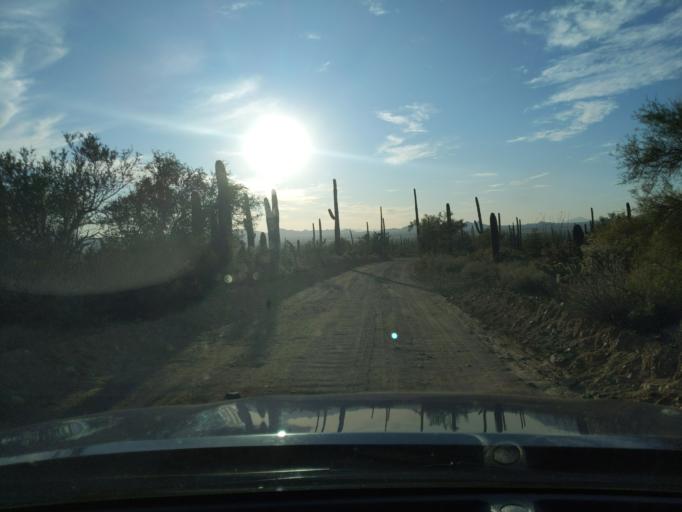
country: US
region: Arizona
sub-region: Pima County
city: Picture Rocks
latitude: 32.2878
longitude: -111.2005
